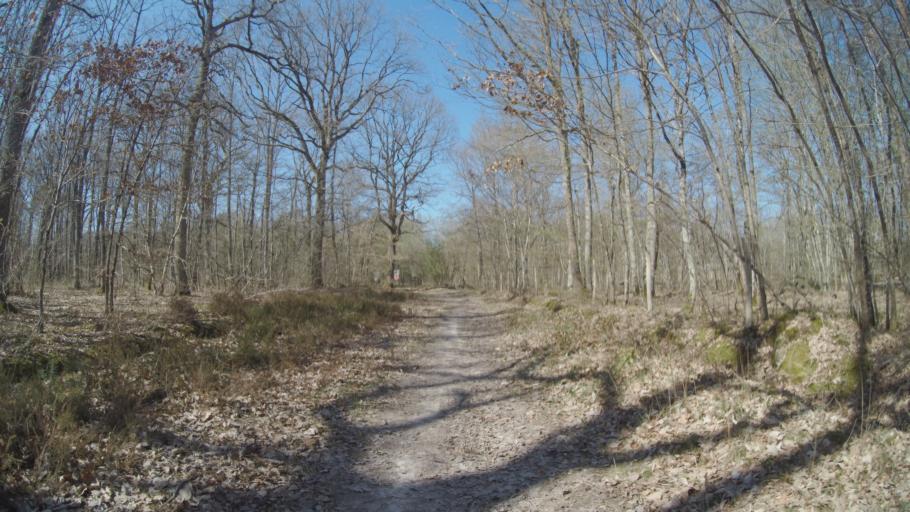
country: FR
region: Centre
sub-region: Departement du Loiret
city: Chanteau
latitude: 47.9561
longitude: 1.9770
